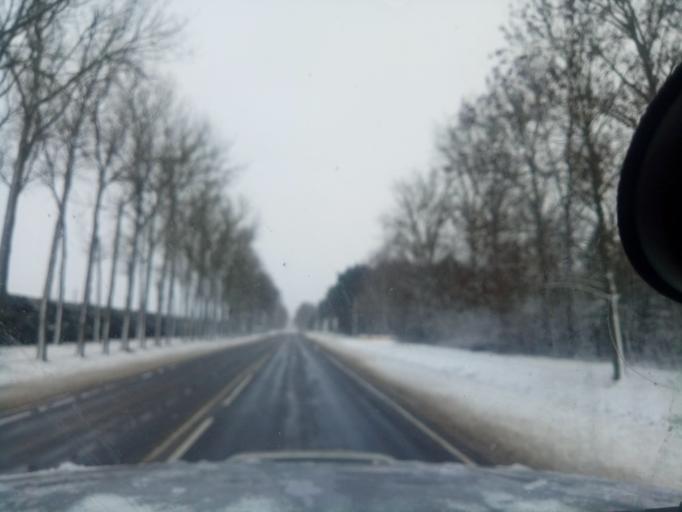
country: BY
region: Minsk
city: Haradzyeya
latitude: 53.3394
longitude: 26.5207
